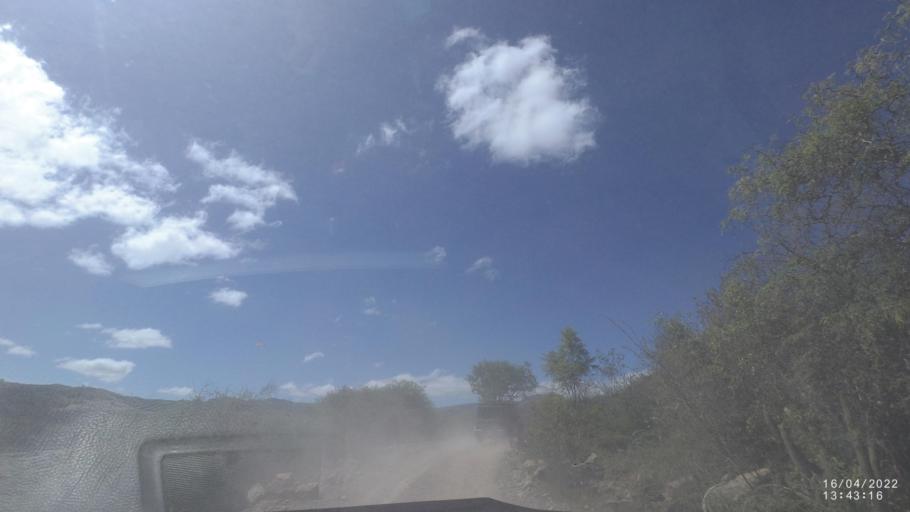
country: BO
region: Cochabamba
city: Mizque
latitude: -17.9974
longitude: -65.5938
